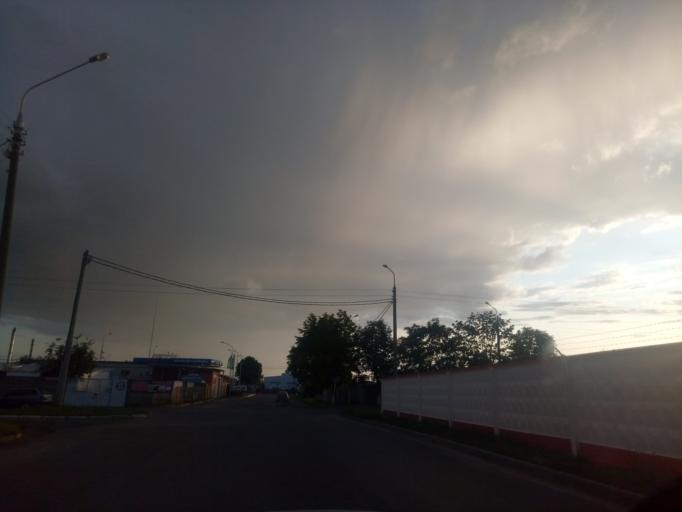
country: BY
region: Minsk
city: Novoye Medvezhino
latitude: 53.8829
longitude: 27.4768
